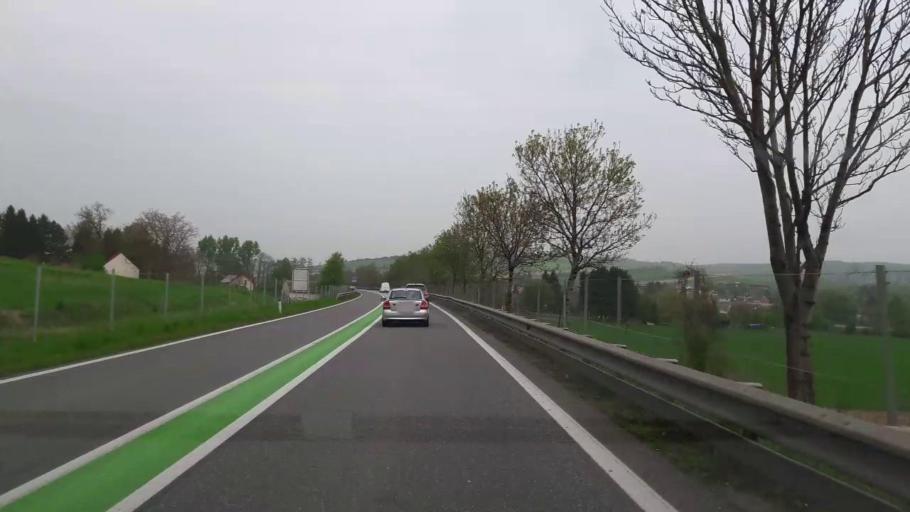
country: AT
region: Lower Austria
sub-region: Politischer Bezirk Hollabrunn
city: Gollersdorf
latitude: 48.4994
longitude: 16.1051
